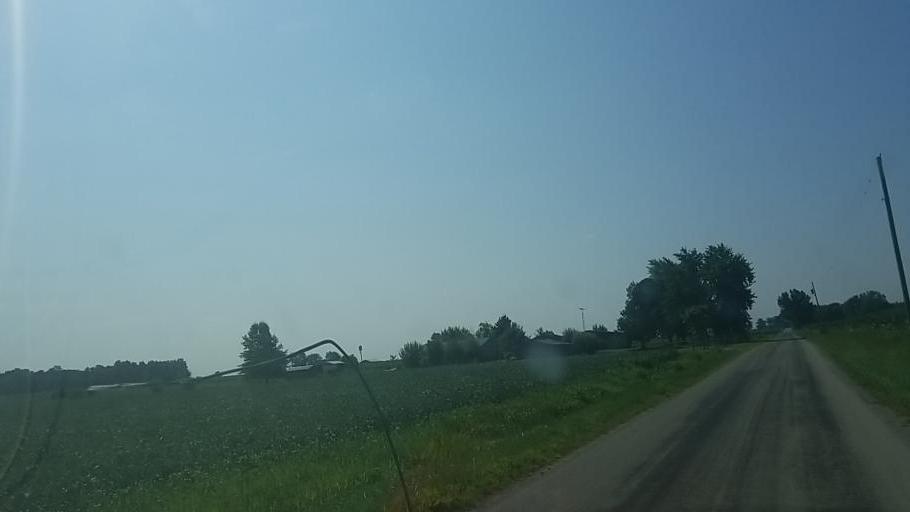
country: US
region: Ohio
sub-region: Marion County
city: Marion
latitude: 40.7056
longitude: -83.1499
